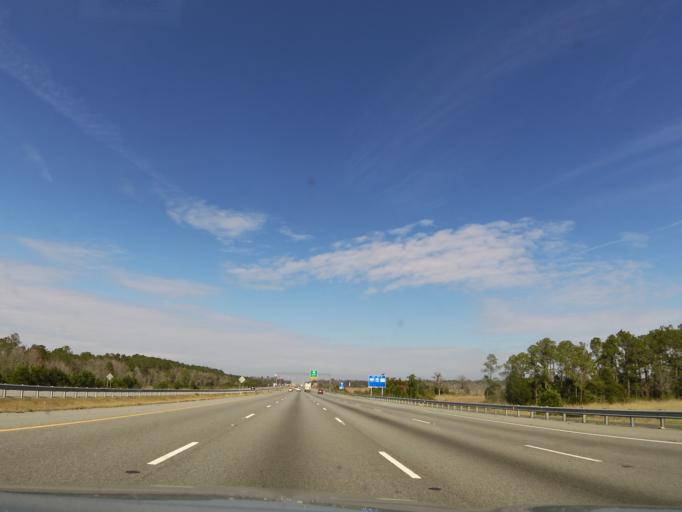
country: US
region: Georgia
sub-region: McIntosh County
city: Darien
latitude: 31.3751
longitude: -81.4544
